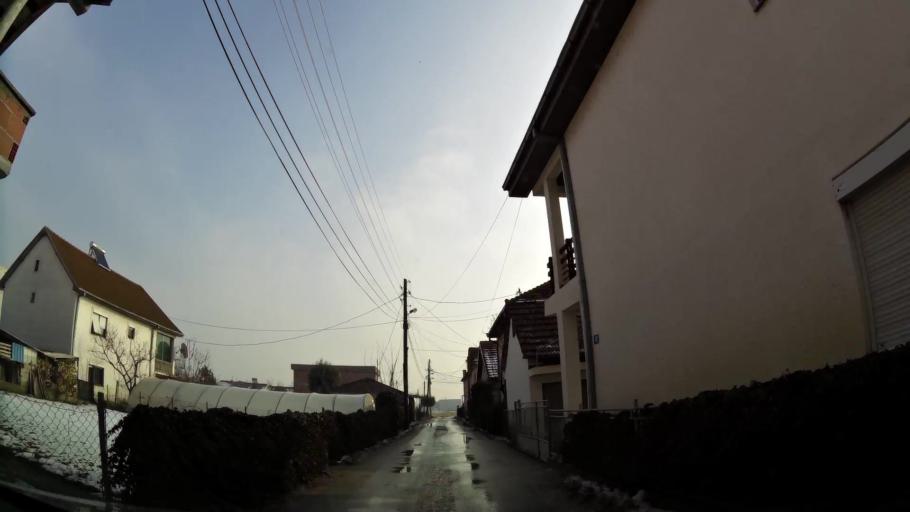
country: MK
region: Ilinden
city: Ilinden
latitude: 41.9876
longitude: 21.5847
